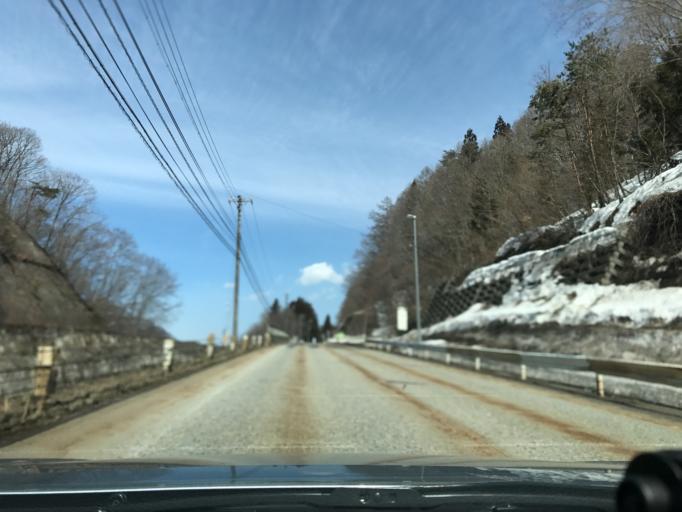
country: JP
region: Nagano
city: Omachi
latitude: 36.5900
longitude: 137.8426
